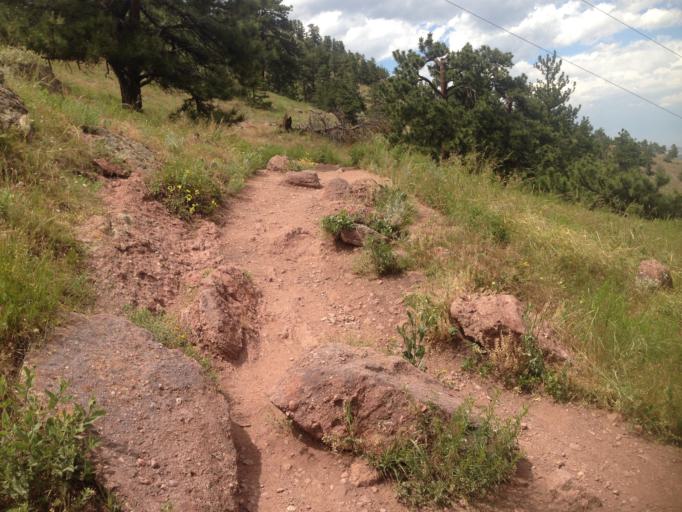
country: US
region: Colorado
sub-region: Boulder County
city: Boulder
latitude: 40.0305
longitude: -105.3035
